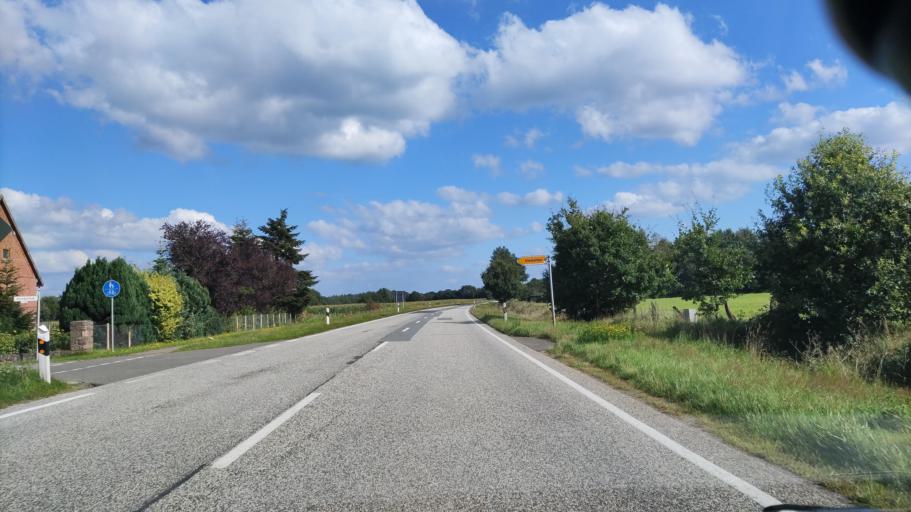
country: DE
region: Schleswig-Holstein
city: Jevenstedt
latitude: 54.2269
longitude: 9.6930
